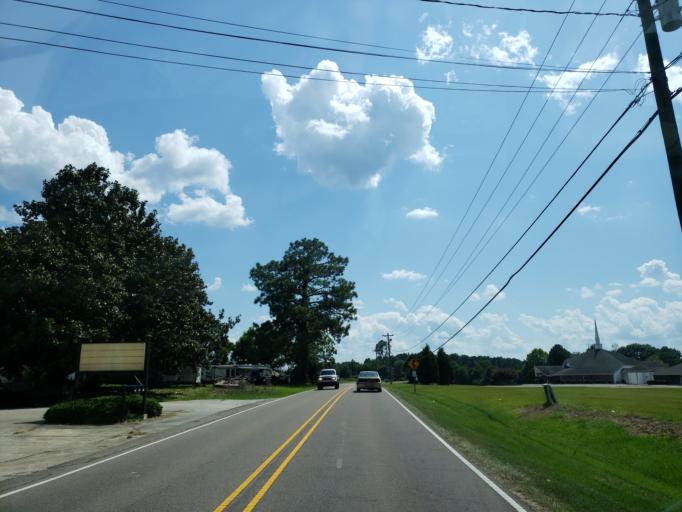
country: US
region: Mississippi
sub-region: Lamar County
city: West Hattiesburg
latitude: 31.2917
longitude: -89.3919
